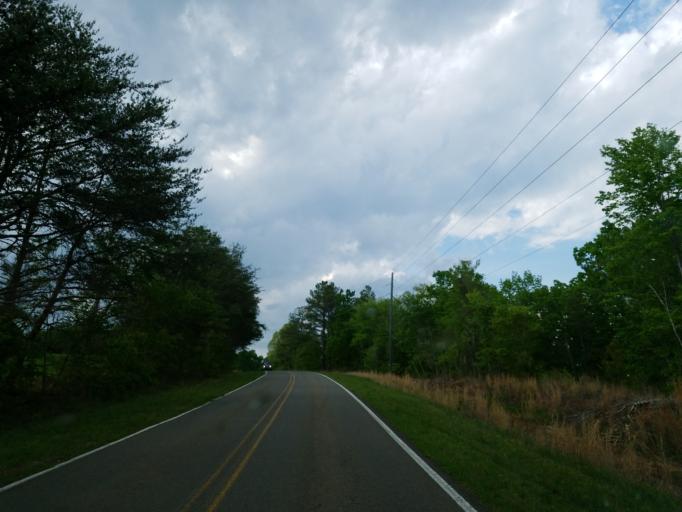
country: US
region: Georgia
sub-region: Pickens County
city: Jasper
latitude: 34.4407
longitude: -84.4508
